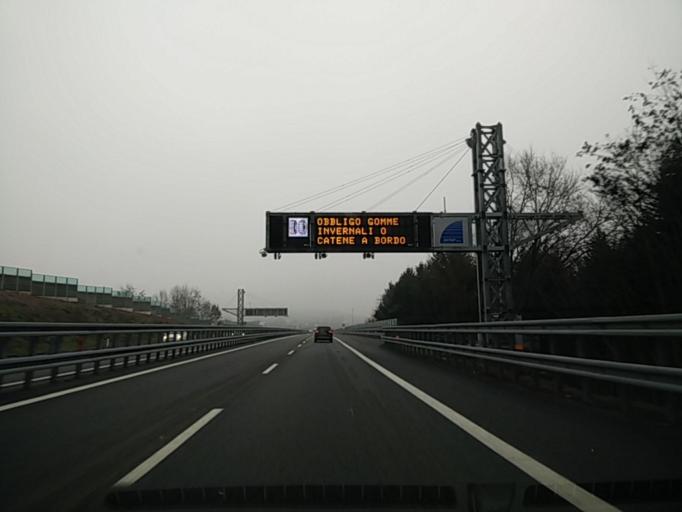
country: IT
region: Piedmont
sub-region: Provincia di Asti
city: Asti
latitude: 44.9150
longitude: 8.2154
